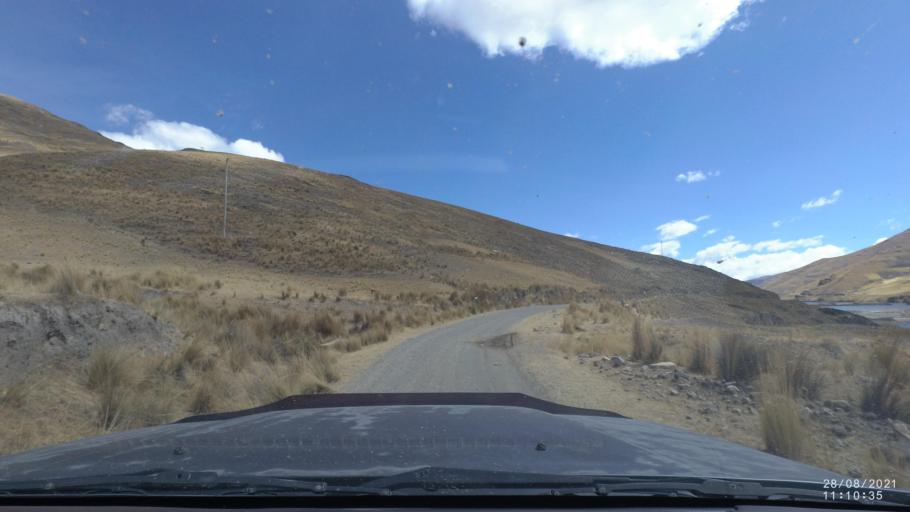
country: BO
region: Cochabamba
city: Cochabamba
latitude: -17.1561
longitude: -66.3119
